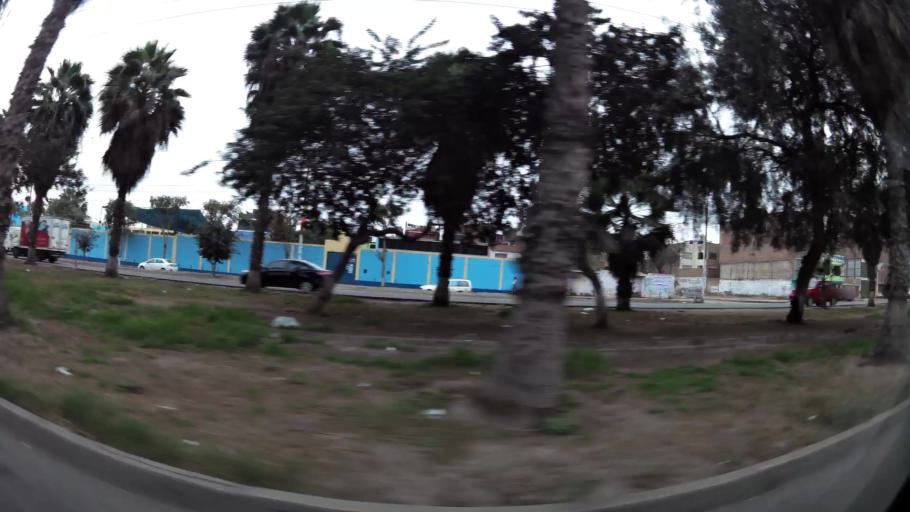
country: PE
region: Lima
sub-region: Lima
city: Independencia
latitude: -11.9323
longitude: -77.0548
